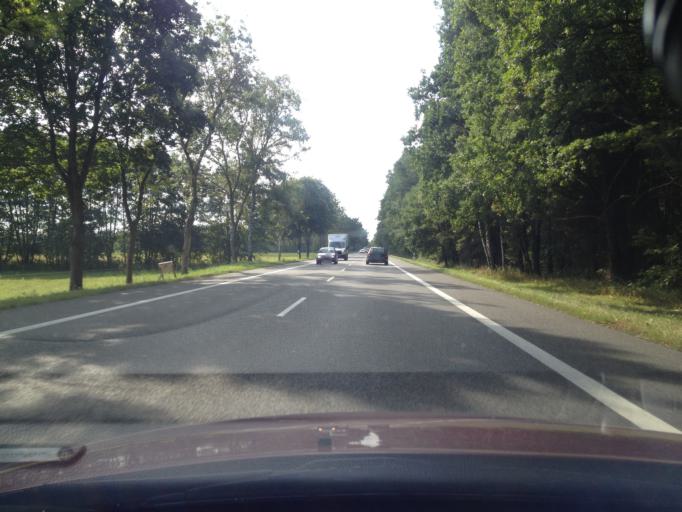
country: PL
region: West Pomeranian Voivodeship
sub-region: Powiat goleniowski
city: Przybiernow
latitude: 53.7761
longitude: 14.7789
